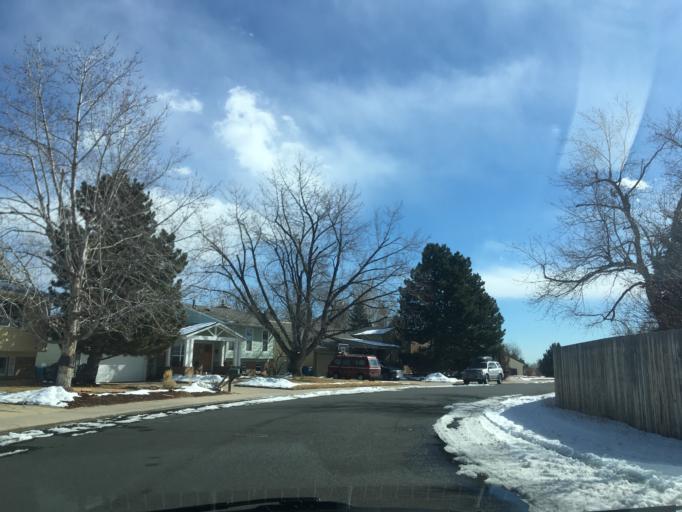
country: US
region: Colorado
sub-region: Boulder County
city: Louisville
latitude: 39.9844
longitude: -105.1622
